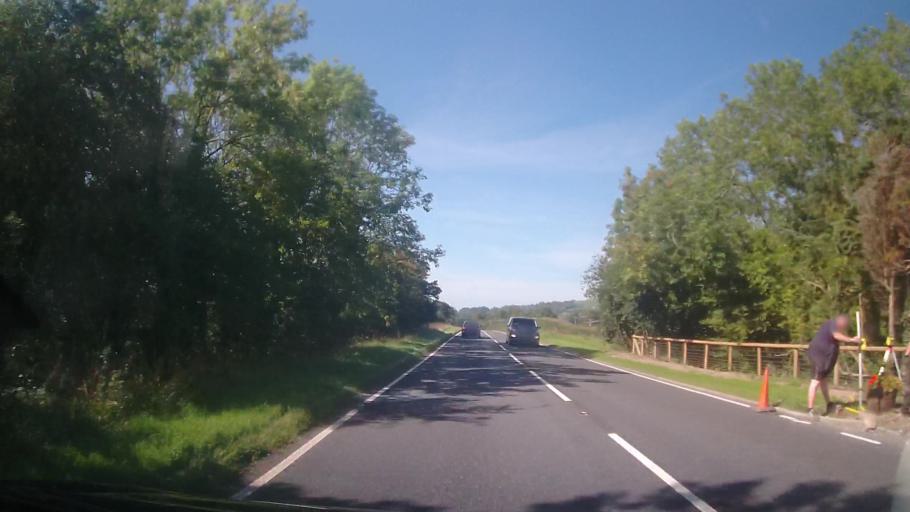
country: GB
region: England
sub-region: Shropshire
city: Bishop's Castle
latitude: 52.5281
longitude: -3.0249
